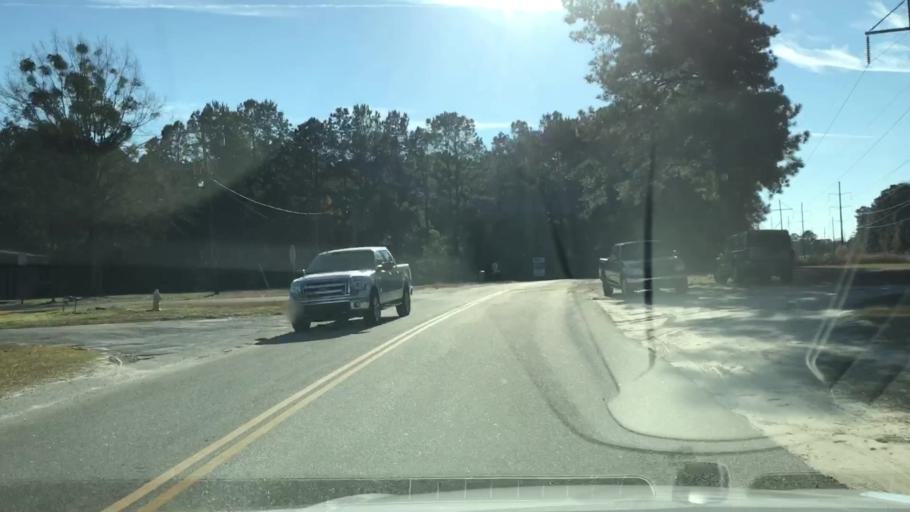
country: US
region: South Carolina
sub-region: Berkeley County
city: Ladson
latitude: 32.9936
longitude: -80.0960
